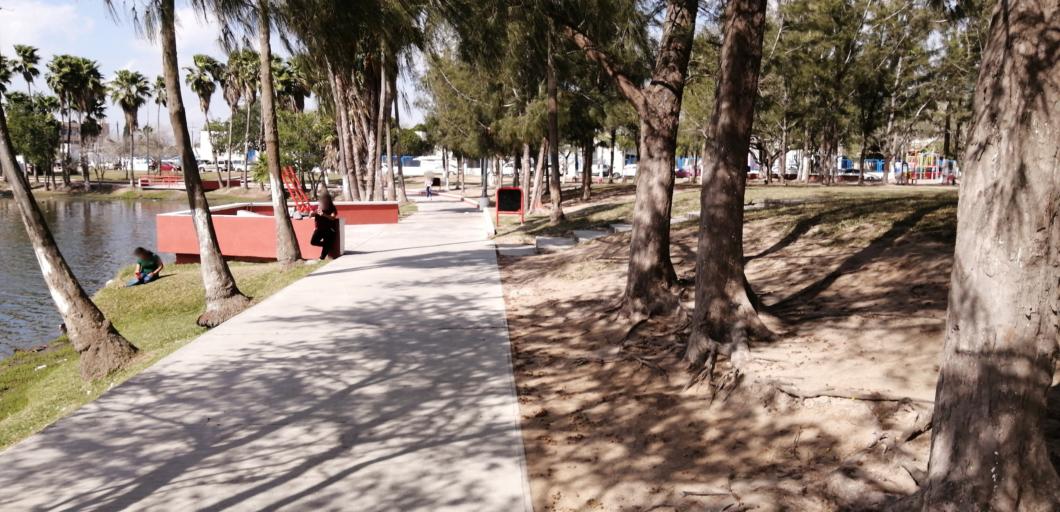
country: MX
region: Tamaulipas
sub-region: Matamoros
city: Heroica Matamoros
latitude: 25.8686
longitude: -97.4949
